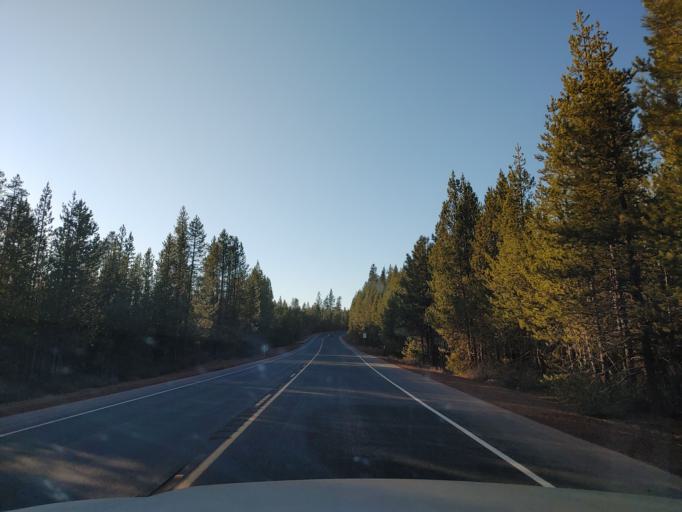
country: US
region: Oregon
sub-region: Deschutes County
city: La Pine
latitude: 43.4415
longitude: -121.8665
